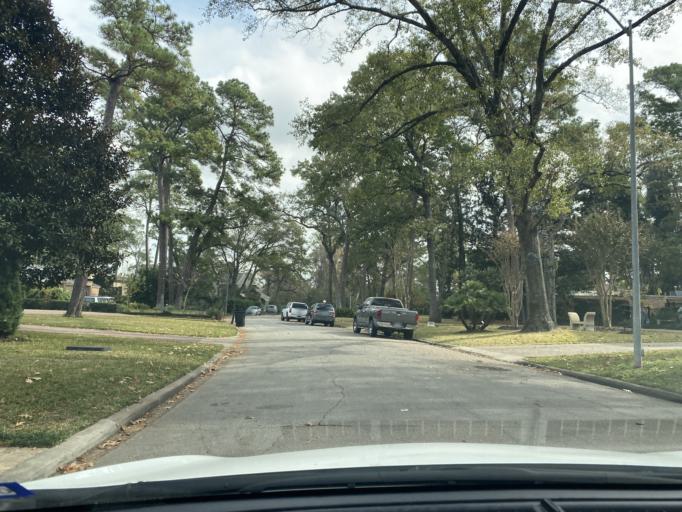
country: US
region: Texas
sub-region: Harris County
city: Hunters Creek Village
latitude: 29.7650
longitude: -95.4633
